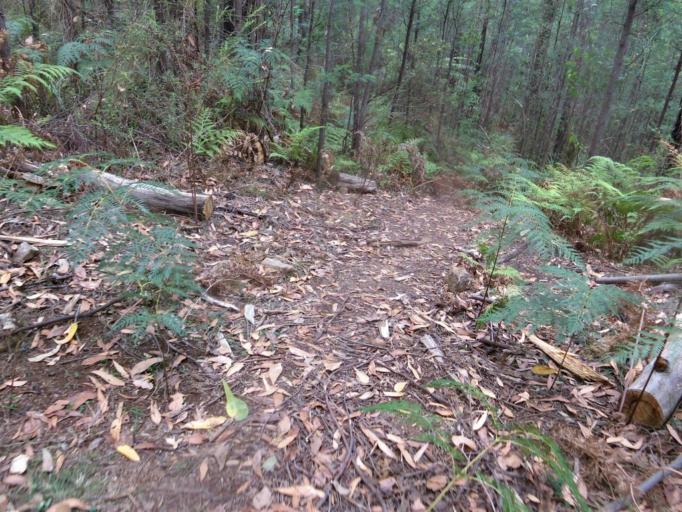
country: AU
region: Victoria
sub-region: Yarra Ranges
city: Healesville
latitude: -37.4313
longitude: 145.5778
